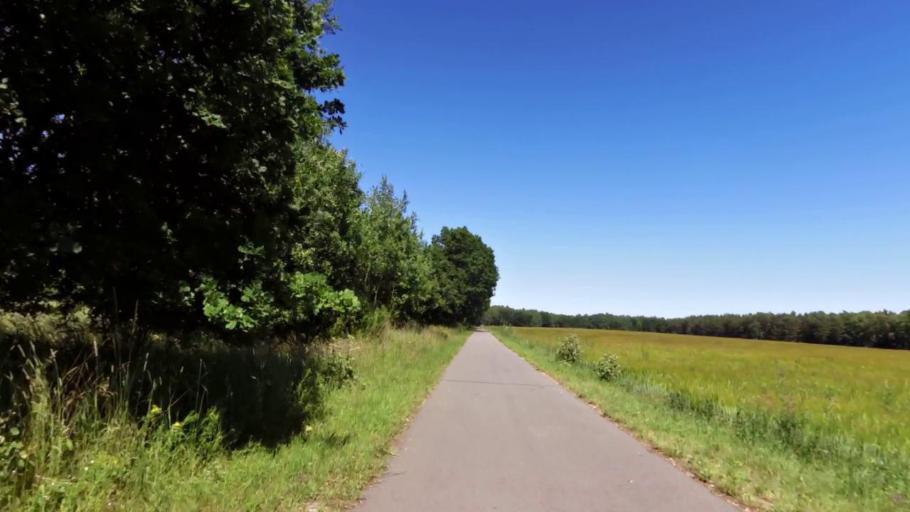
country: PL
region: West Pomeranian Voivodeship
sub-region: Powiat kolobrzeski
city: Goscino
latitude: 54.0367
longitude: 15.7124
